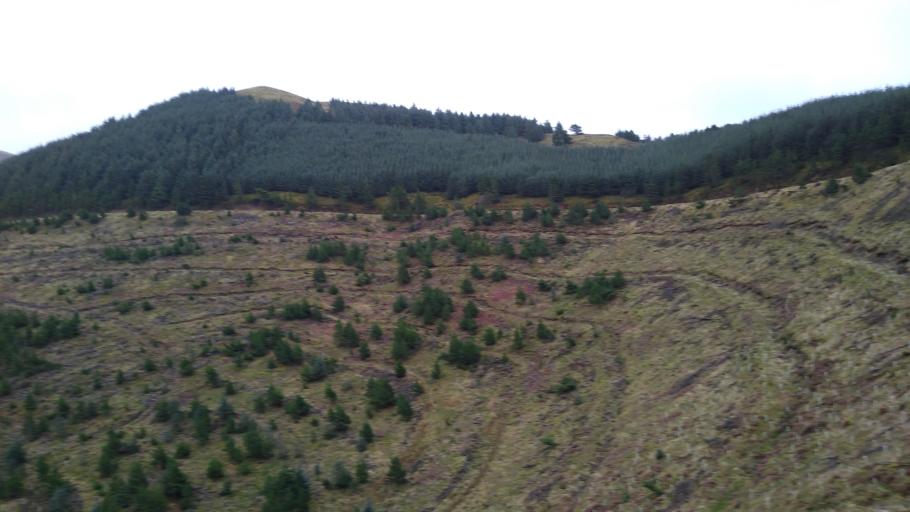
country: GB
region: England
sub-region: Cumbria
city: Frizington
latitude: 54.5580
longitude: -3.3955
